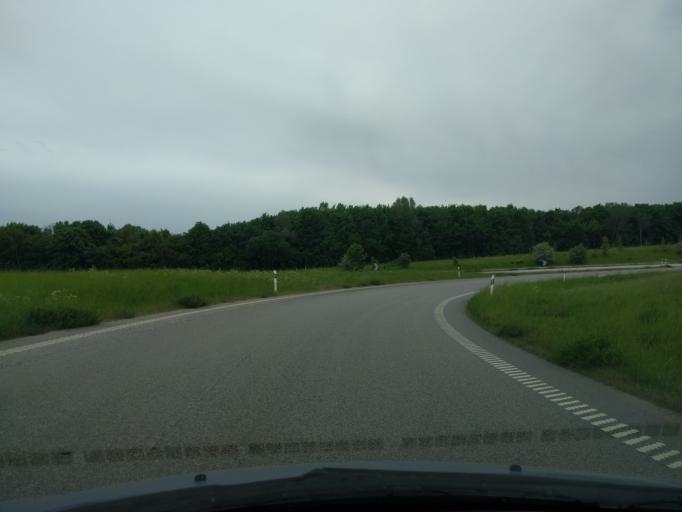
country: SE
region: Skane
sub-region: Malmo
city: Oxie
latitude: 55.5554
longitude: 13.1044
